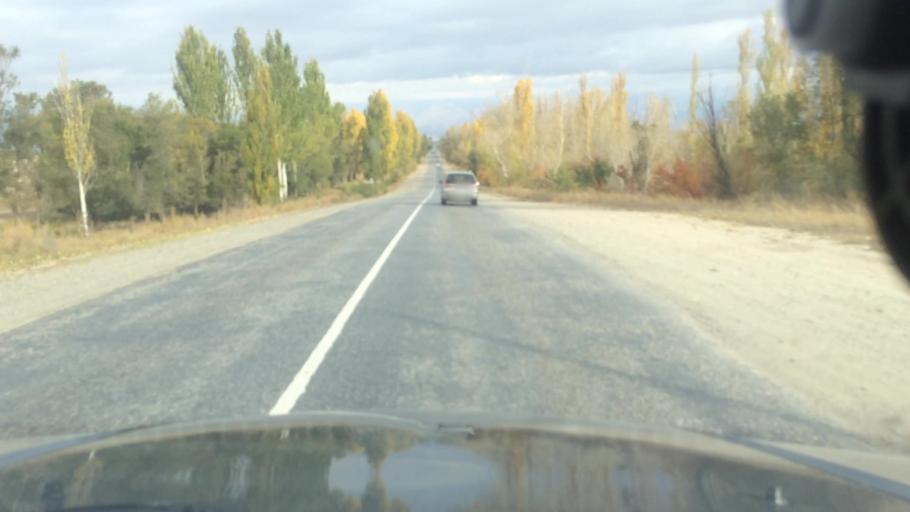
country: KG
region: Ysyk-Koel
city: Tyup
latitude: 42.6108
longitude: 78.3671
